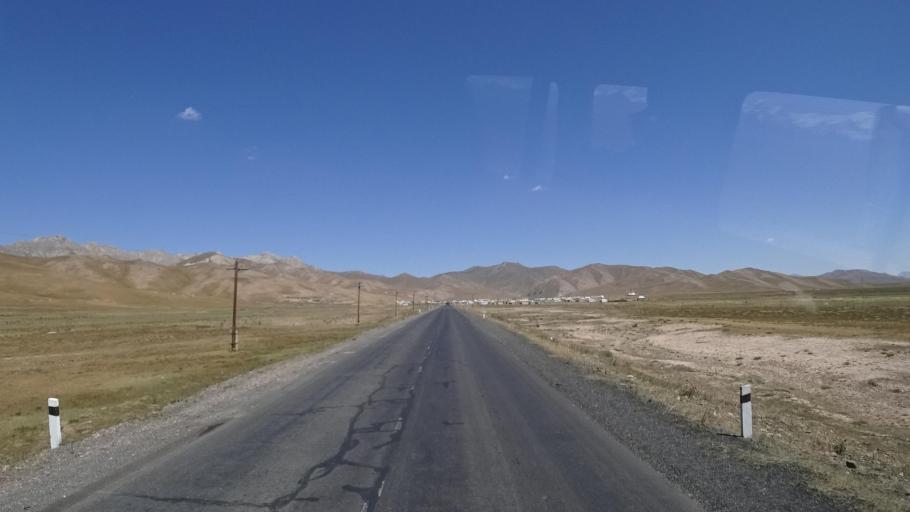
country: KG
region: Osh
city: Gul'cha
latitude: 39.7157
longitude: 73.2402
